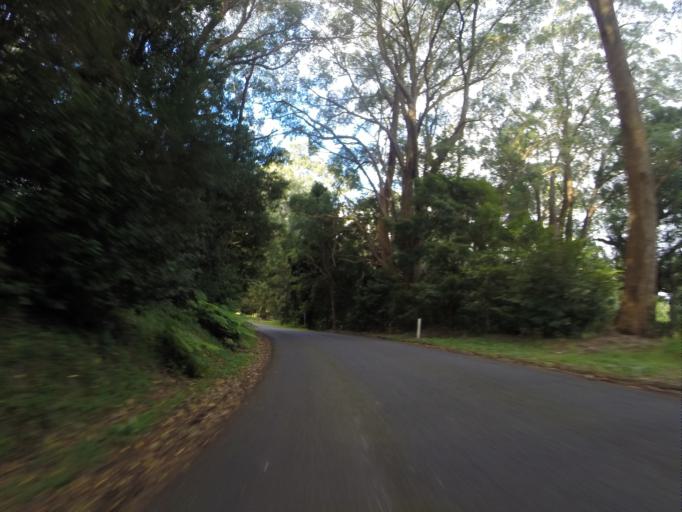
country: AU
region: New South Wales
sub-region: Shoalhaven Shire
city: Kangaroo Valley
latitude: -34.6073
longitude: 150.5420
